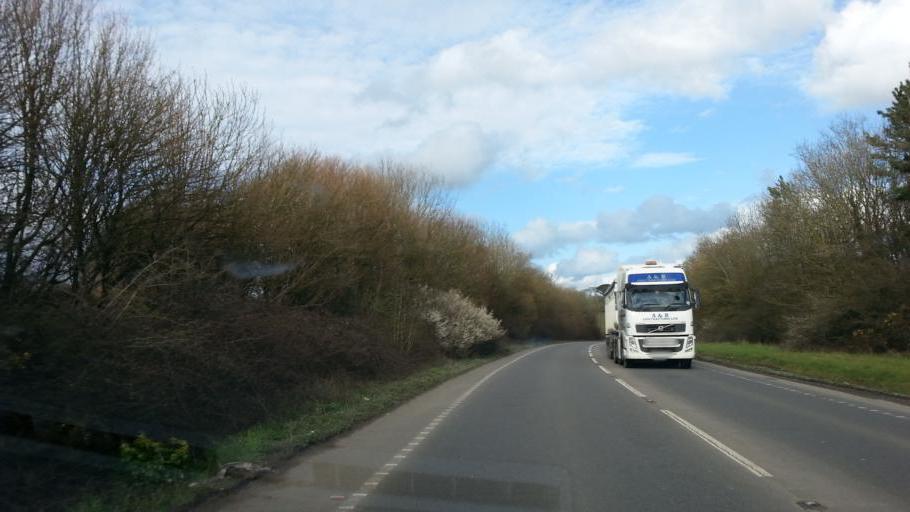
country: GB
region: England
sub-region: Devon
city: Northam
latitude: 51.0284
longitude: -4.2277
